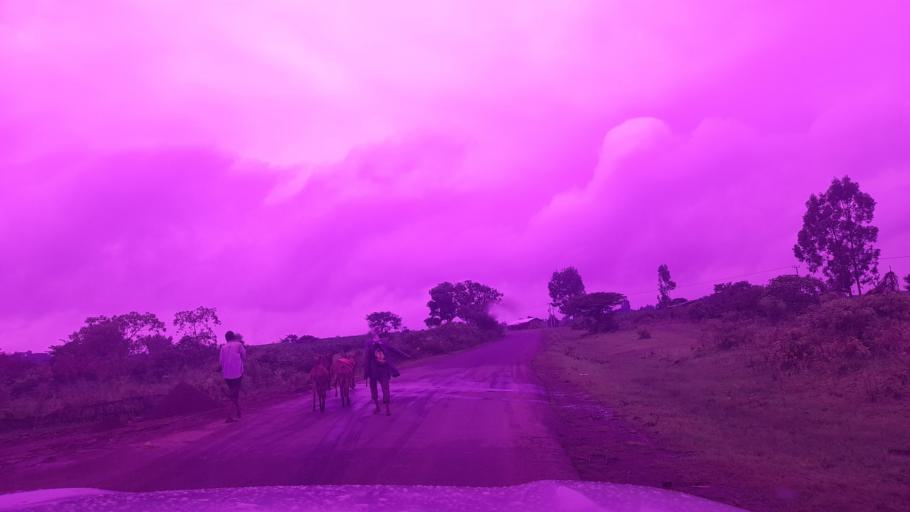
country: ET
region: Oromiya
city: Jima
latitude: 7.6893
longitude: 37.2314
